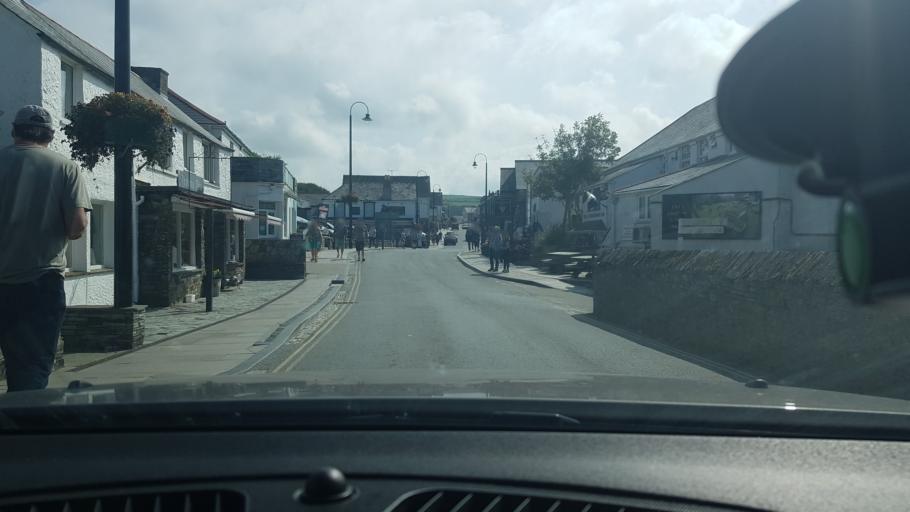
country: GB
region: England
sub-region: Cornwall
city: Tintagel
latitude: 50.6639
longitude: -4.7528
